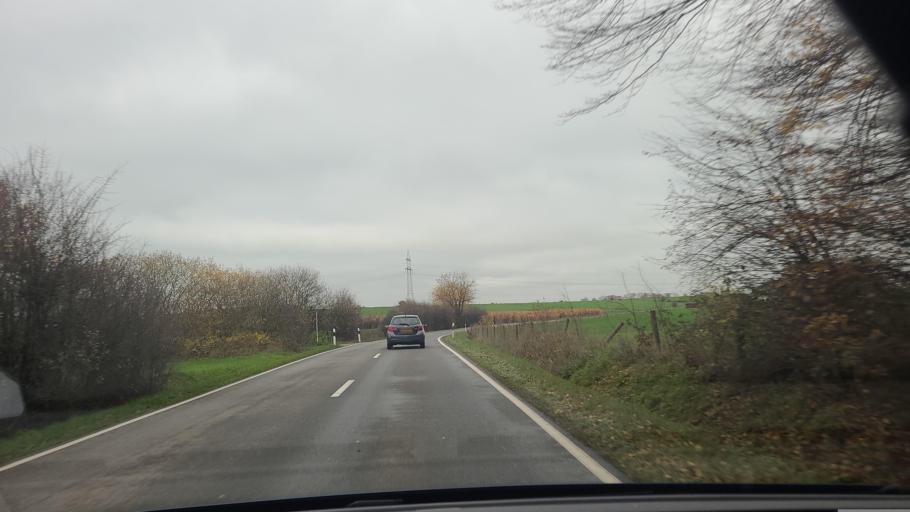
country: LU
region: Luxembourg
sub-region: Canton d'Esch-sur-Alzette
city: Mondercange
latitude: 49.5514
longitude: 5.9690
